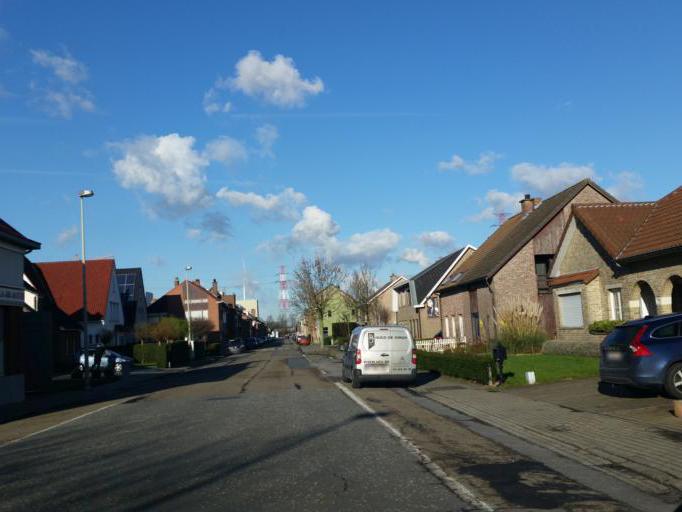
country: BE
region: Flanders
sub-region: Provincie Oost-Vlaanderen
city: Beveren
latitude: 51.2551
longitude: 4.2760
